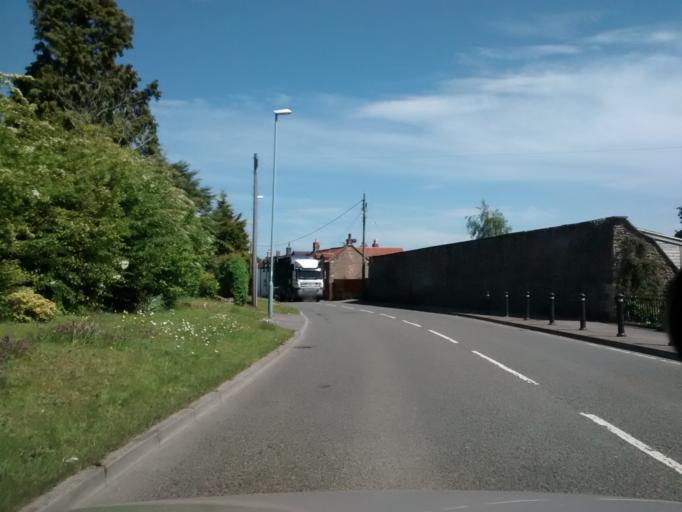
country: GB
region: England
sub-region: Bath and North East Somerset
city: Clutton
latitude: 51.3108
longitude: -2.5269
